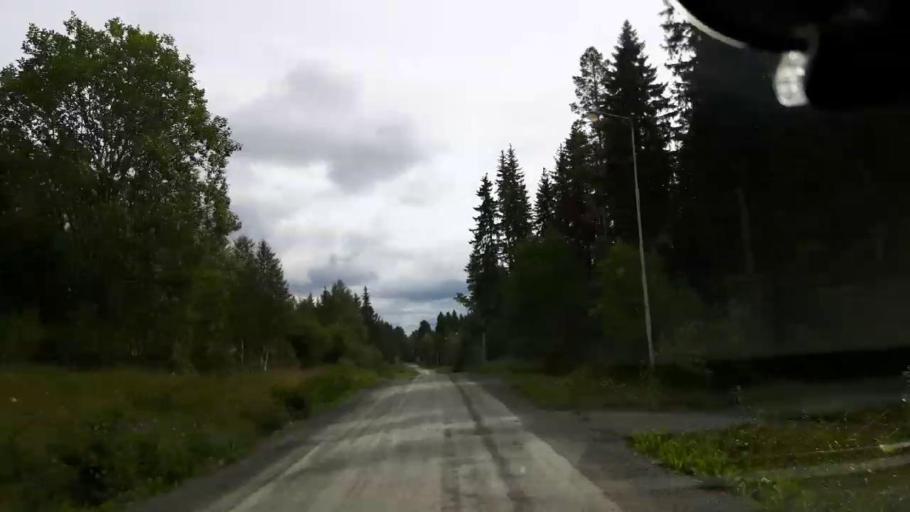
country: SE
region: Jaemtland
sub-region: Krokoms Kommun
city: Valla
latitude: 63.6280
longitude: 14.0240
